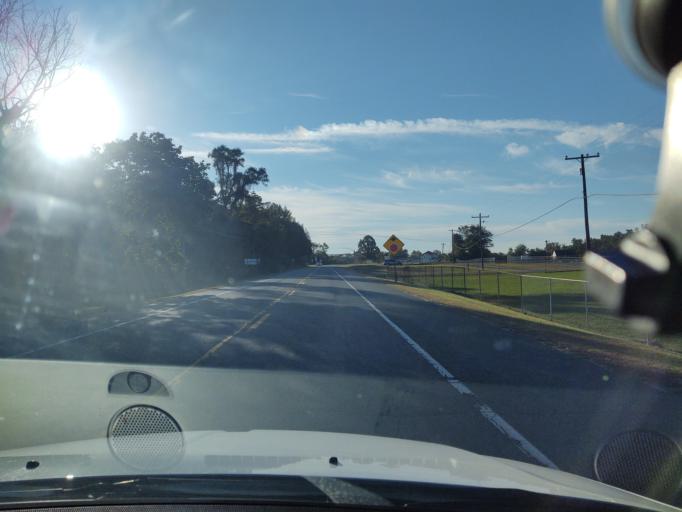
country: US
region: Maryland
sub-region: Queen Anne's County
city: Kingstown
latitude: 39.2343
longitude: -75.9155
